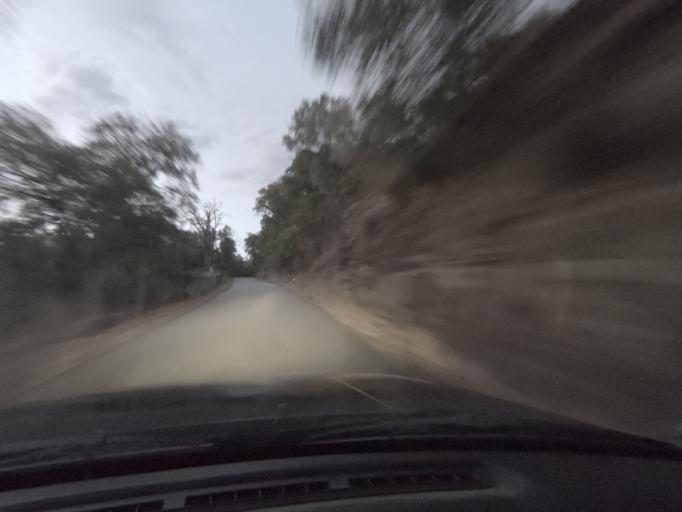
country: PT
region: Vila Real
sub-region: Mesao Frio
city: Mesao Frio
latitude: 41.1596
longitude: -7.8406
